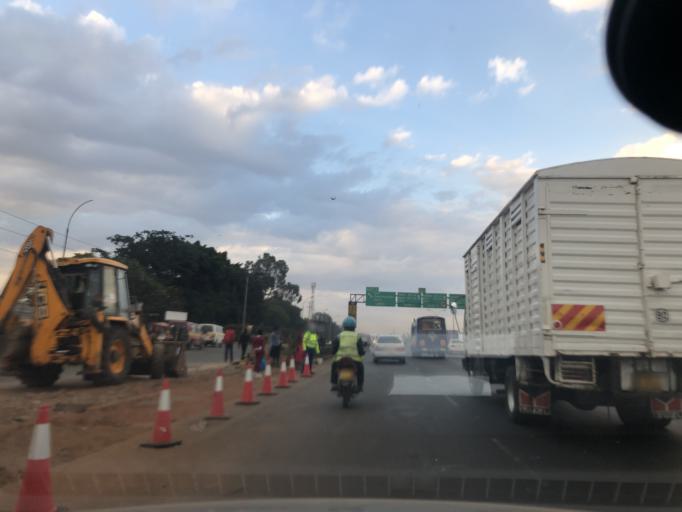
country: KE
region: Nairobi Area
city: Pumwani
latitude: -1.2484
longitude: 36.8633
